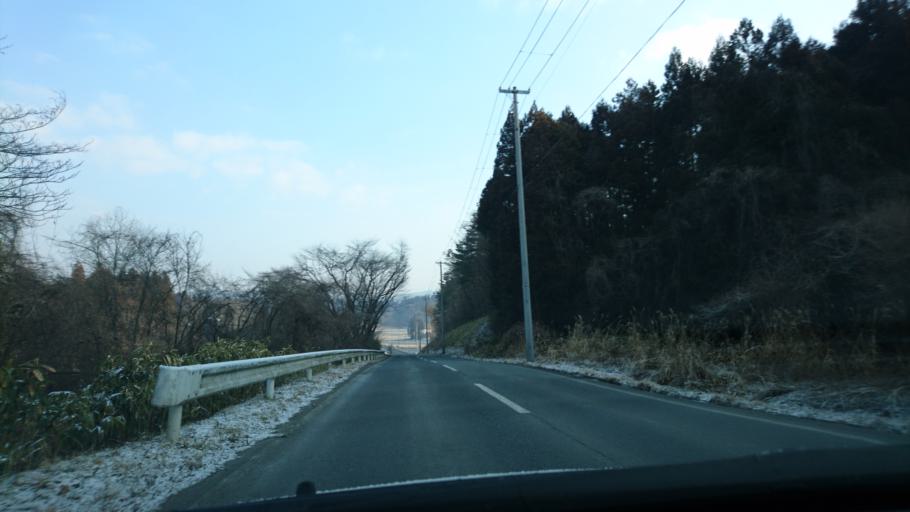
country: JP
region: Iwate
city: Ichinoseki
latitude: 38.9206
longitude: 141.3841
